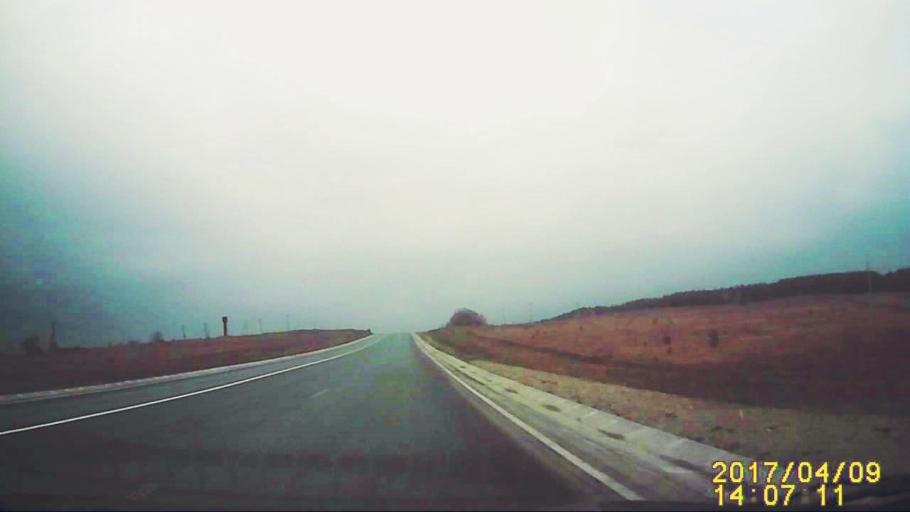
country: RU
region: Ulyanovsk
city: Silikatnyy
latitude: 54.0093
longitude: 48.2189
